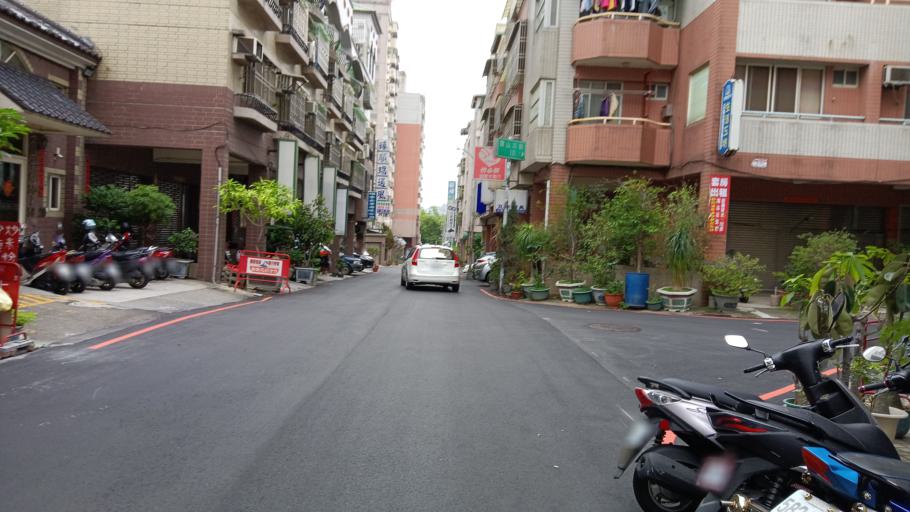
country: TW
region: Taiwan
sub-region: Taichung City
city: Taichung
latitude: 24.1519
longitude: 120.6139
